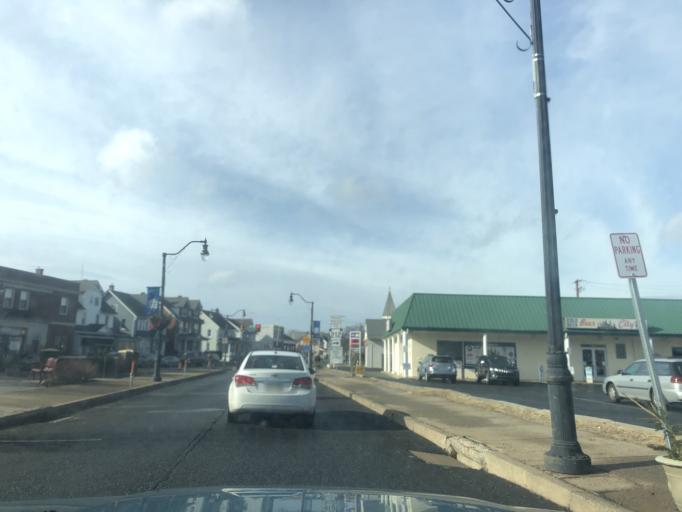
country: US
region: Pennsylvania
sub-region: Bucks County
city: Quakertown
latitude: 40.4414
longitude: -75.3379
